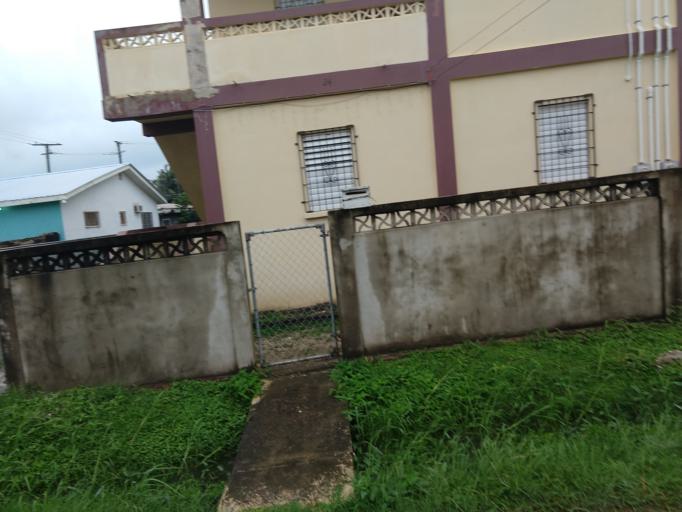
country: BZ
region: Belize
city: Belize City
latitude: 17.5041
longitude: -88.1909
